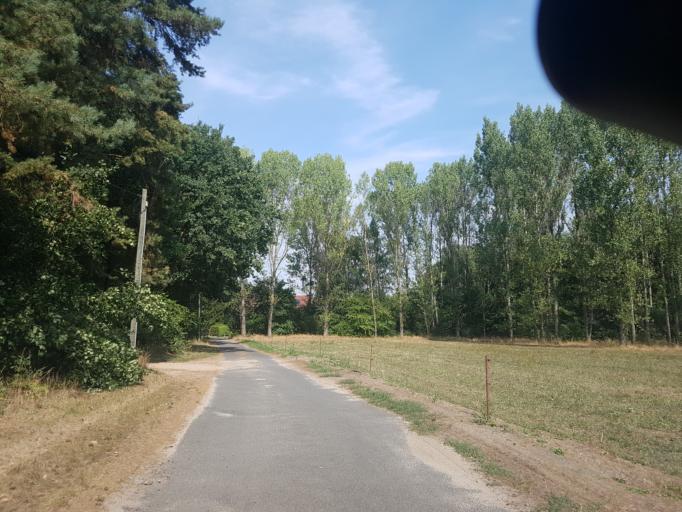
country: DE
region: Brandenburg
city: Treuenbrietzen
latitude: 52.0789
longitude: 12.8342
